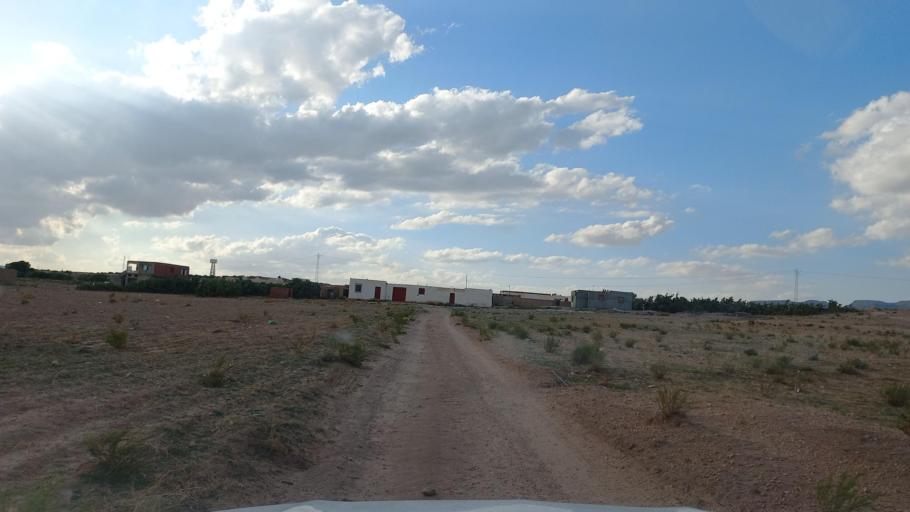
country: TN
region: Al Qasrayn
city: Sbiba
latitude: 35.3888
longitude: 9.0533
